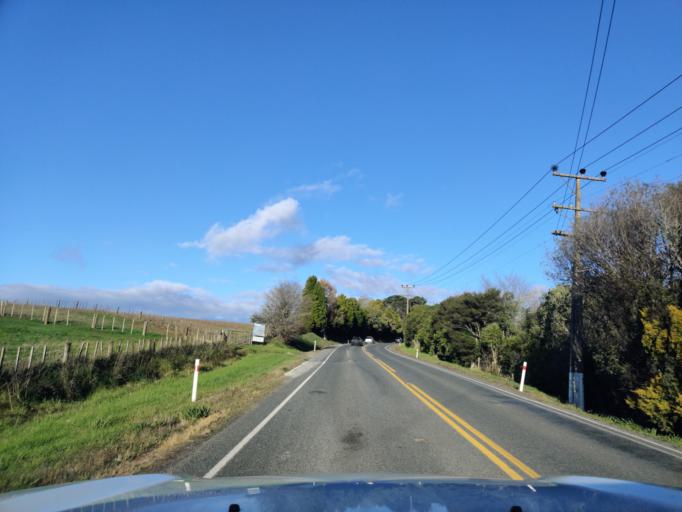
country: NZ
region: Auckland
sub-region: Auckland
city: Red Hill
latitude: -36.9642
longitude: 174.9803
